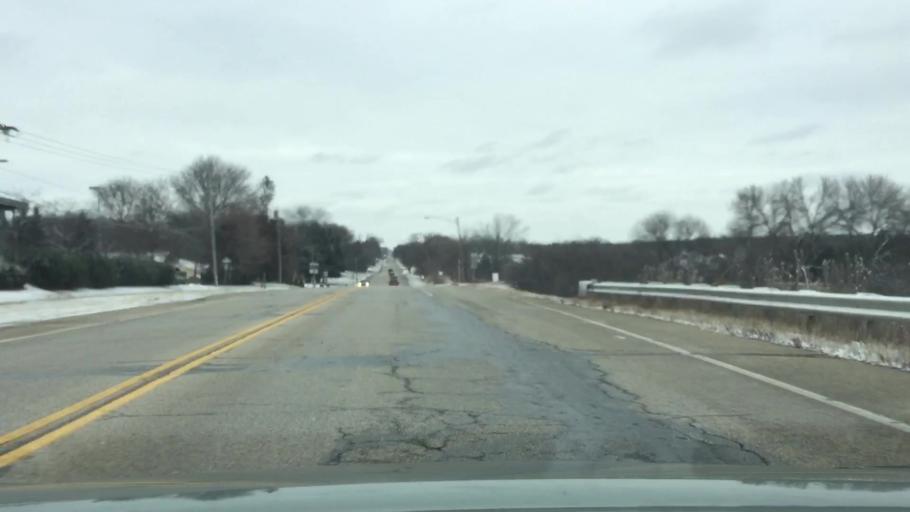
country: US
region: Wisconsin
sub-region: Waukesha County
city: Brookfield
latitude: 43.0903
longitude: -88.1058
